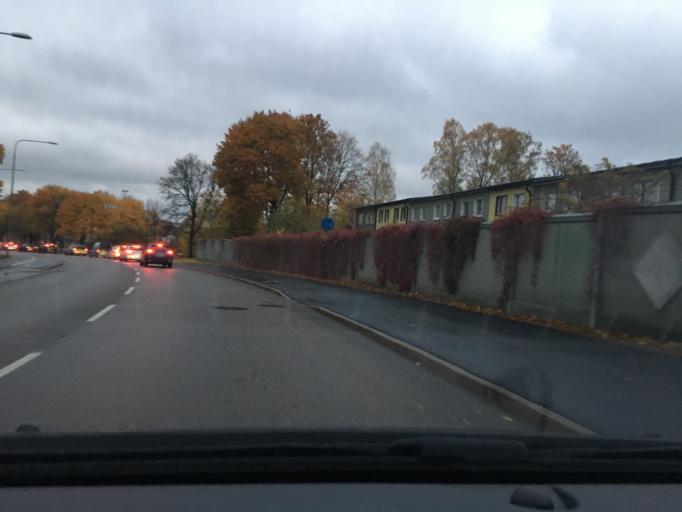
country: SE
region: Stockholm
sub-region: Stockholms Kommun
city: Kista
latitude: 59.3749
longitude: 17.9036
